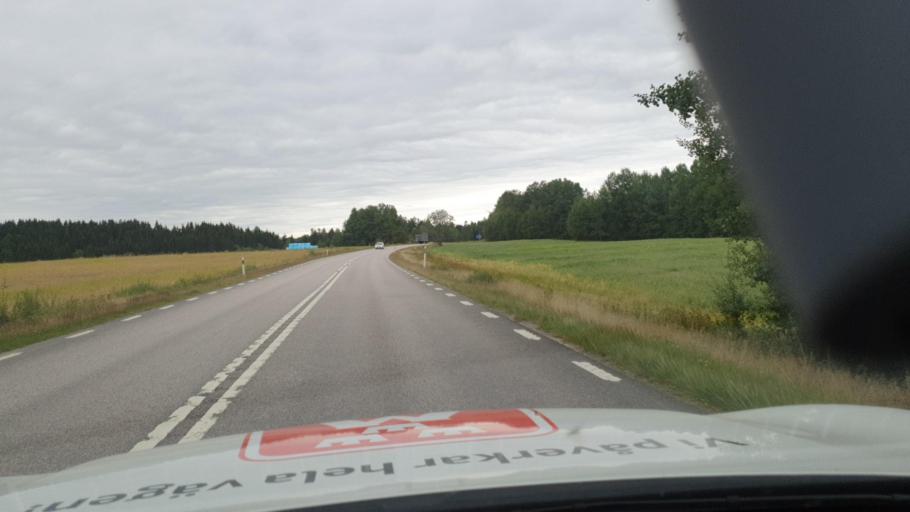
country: SE
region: Vaestra Goetaland
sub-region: Dals-Ed Kommun
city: Ed
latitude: 58.8833
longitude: 11.9049
